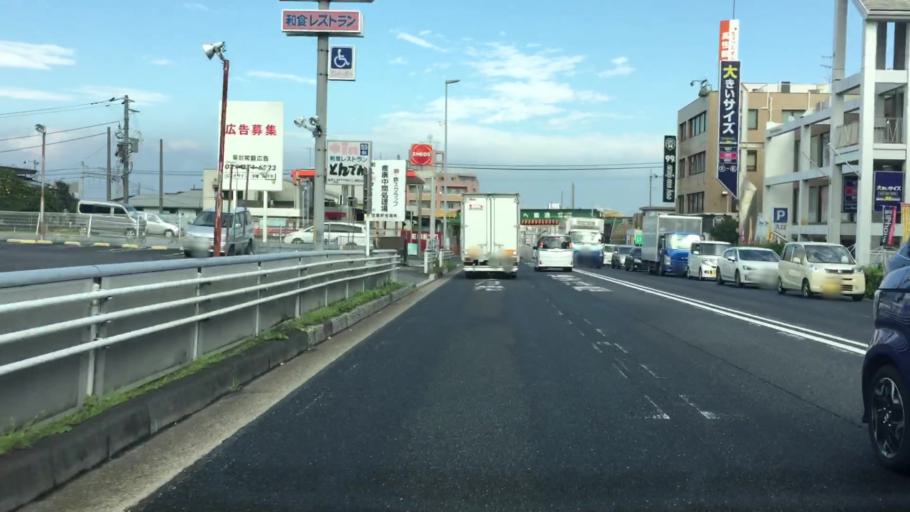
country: JP
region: Chiba
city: Matsudo
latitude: 35.7876
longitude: 139.9096
